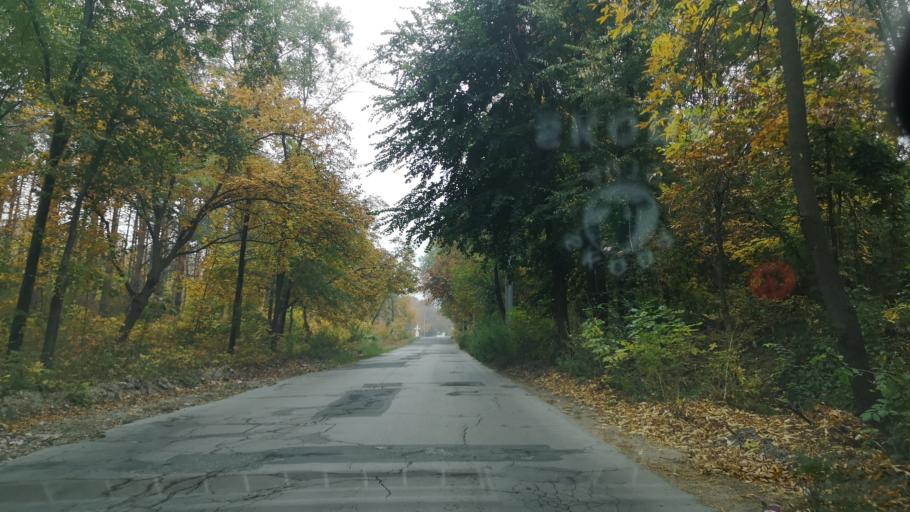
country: MD
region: Chisinau
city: Singera
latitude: 46.9426
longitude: 28.9290
